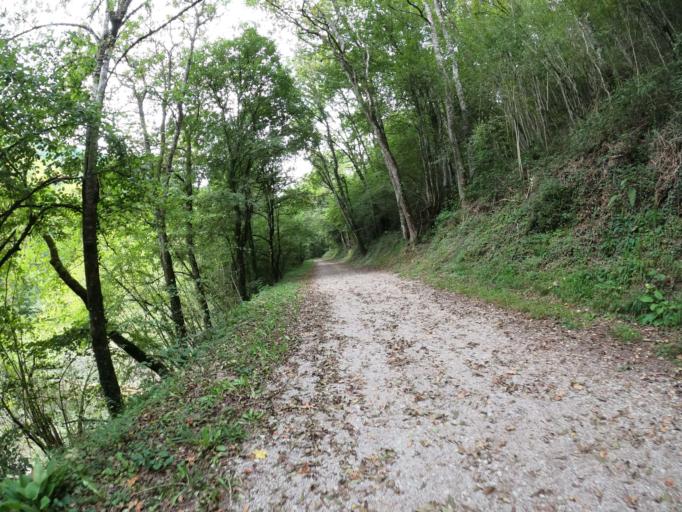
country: ES
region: Navarre
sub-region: Provincia de Navarra
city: Lekunberri
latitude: 42.9806
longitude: -1.8603
